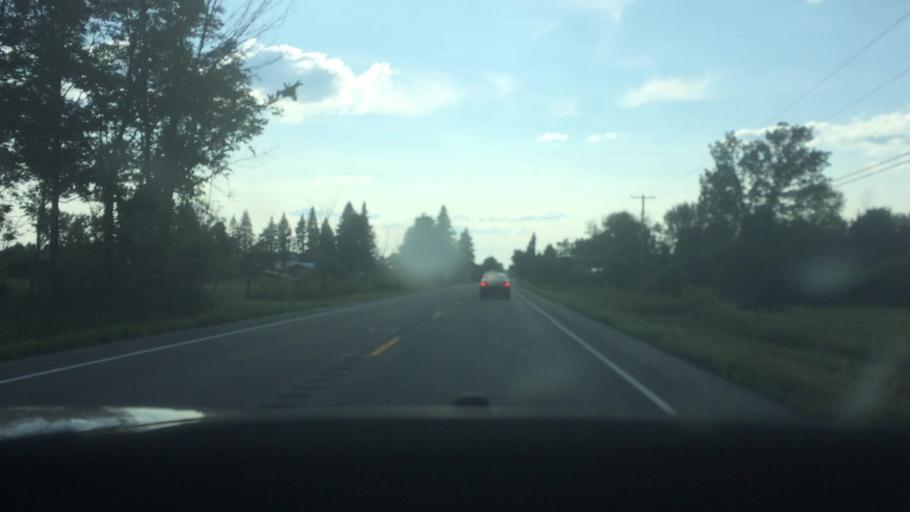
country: US
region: New York
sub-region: St. Lawrence County
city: Potsdam
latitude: 44.6877
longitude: -74.7712
